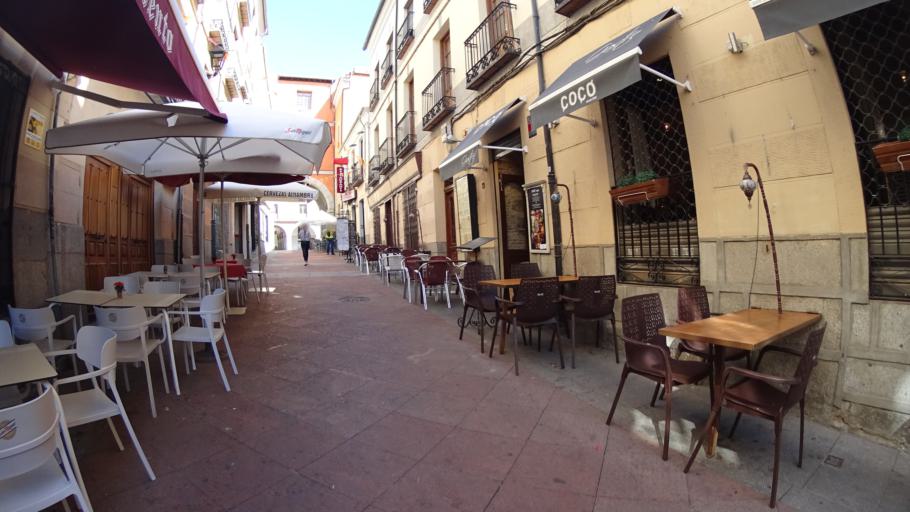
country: ES
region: Castille and Leon
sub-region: Provincia de Avila
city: Avila
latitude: 40.6566
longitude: -4.7009
